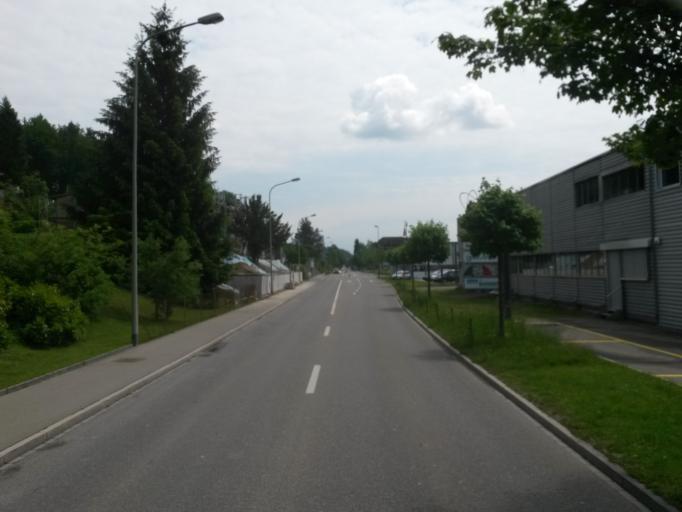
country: CH
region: Zurich
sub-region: Bezirk Pfaeffikon
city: Illnau
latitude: 47.4135
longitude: 8.7220
